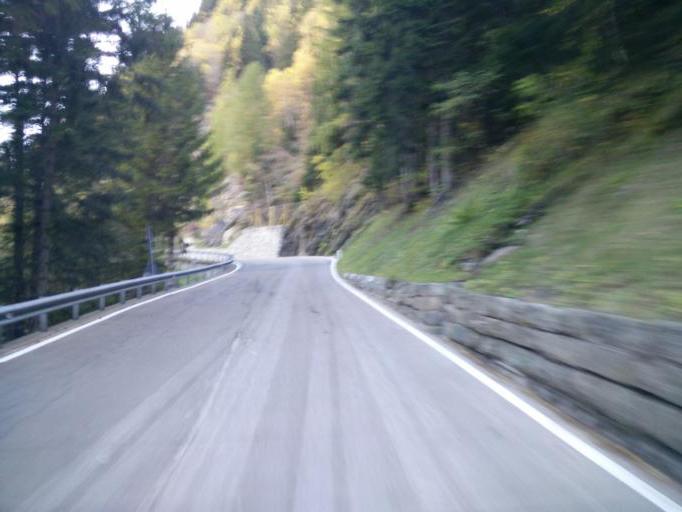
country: IT
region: Trentino-Alto Adige
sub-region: Bolzano
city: Moso in Passiria
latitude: 46.8362
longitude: 11.1701
